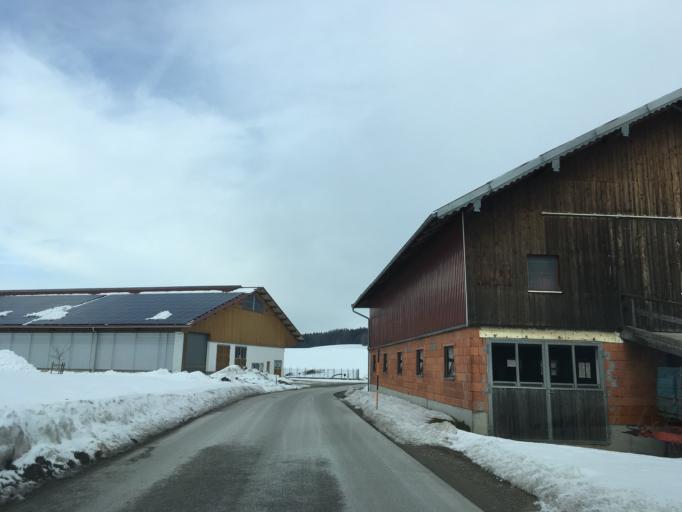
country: DE
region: Bavaria
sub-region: Upper Bavaria
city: Schnaitsee
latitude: 48.0621
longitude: 12.3555
